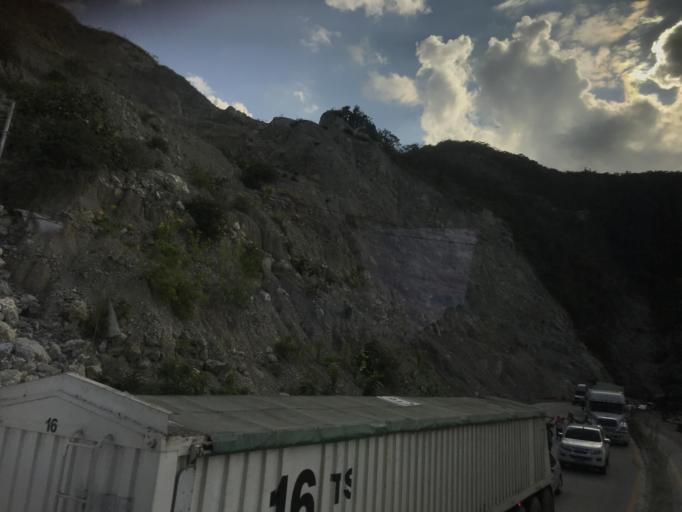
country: GT
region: El Progreso
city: Guastatoya
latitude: 14.8453
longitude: -90.1282
